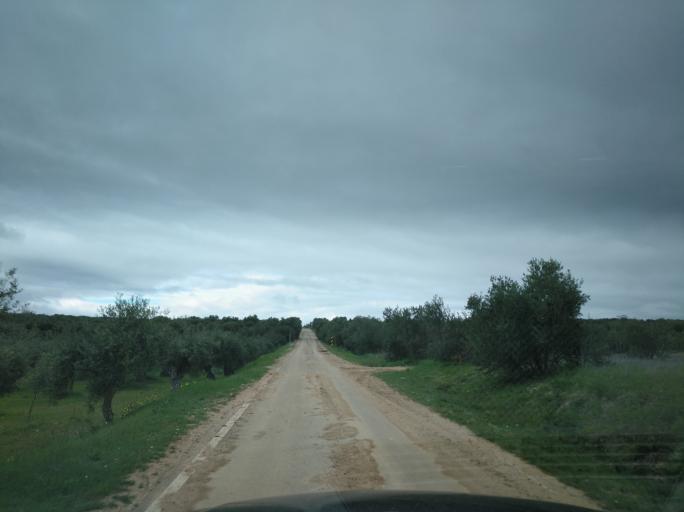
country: PT
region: Portalegre
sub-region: Campo Maior
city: Campo Maior
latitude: 38.9848
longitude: -7.0380
